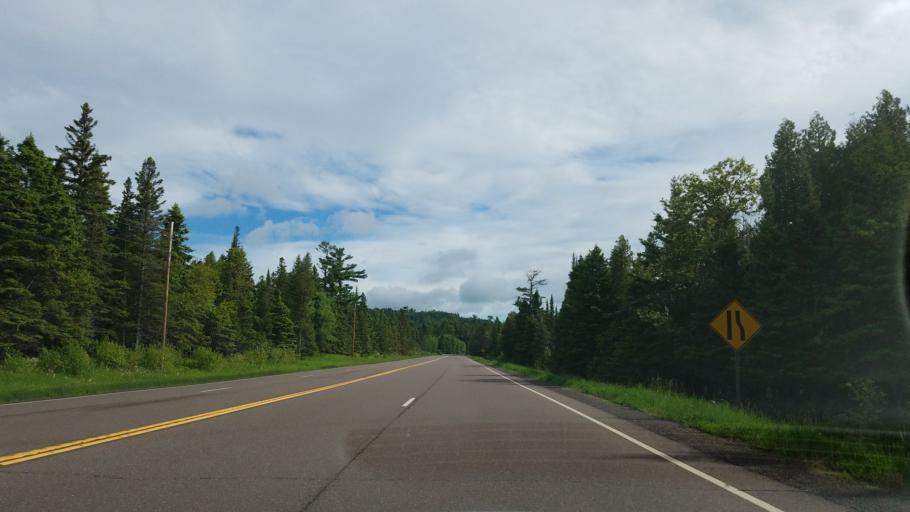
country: US
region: Minnesota
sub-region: Lake County
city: Two Harbors
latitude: 47.0890
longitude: -91.5784
